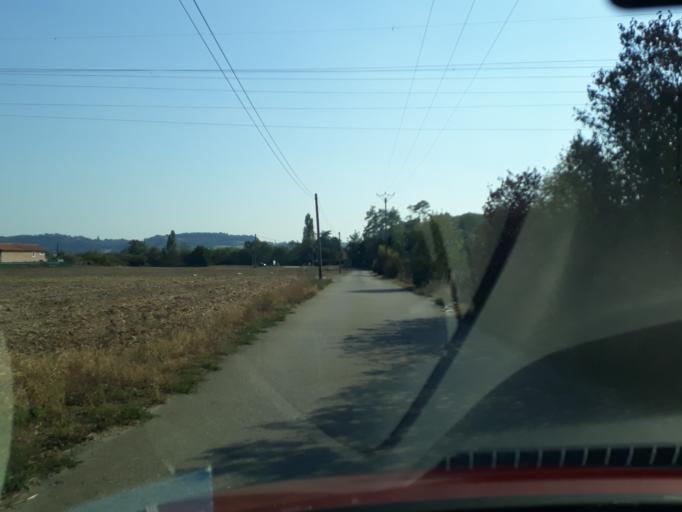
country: FR
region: Rhone-Alpes
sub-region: Departement du Rhone
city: Toussieu
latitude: 45.6666
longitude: 4.9942
